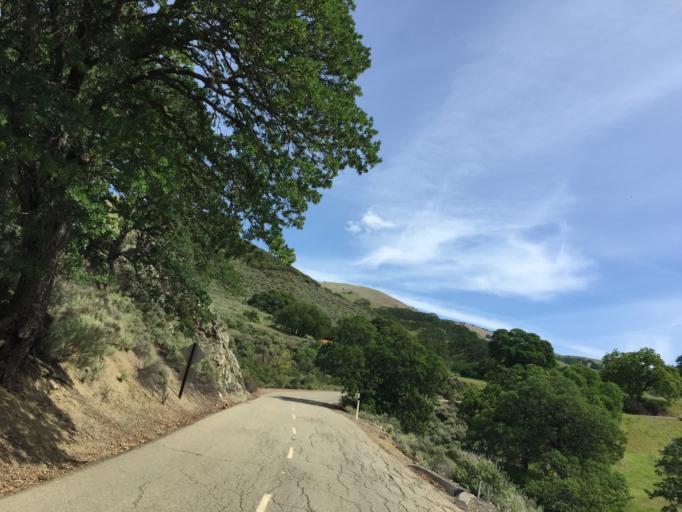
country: US
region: California
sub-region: Contra Costa County
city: Diablo
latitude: 37.8827
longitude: -121.9724
